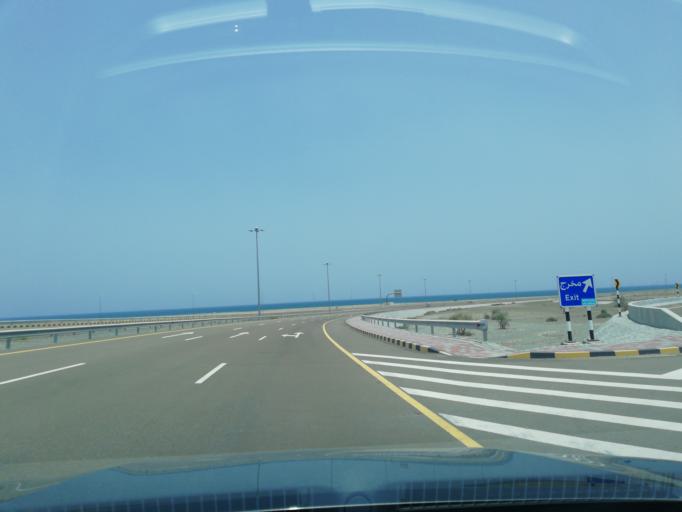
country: AE
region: Al Fujayrah
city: Al Fujayrah
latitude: 24.9535
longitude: 56.3739
